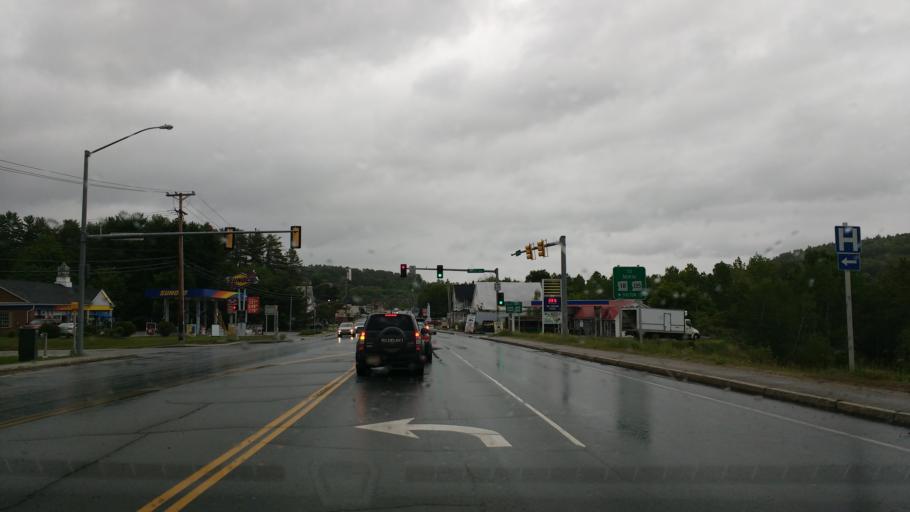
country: US
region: New Hampshire
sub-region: Grafton County
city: Littleton
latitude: 44.3084
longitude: -71.7975
